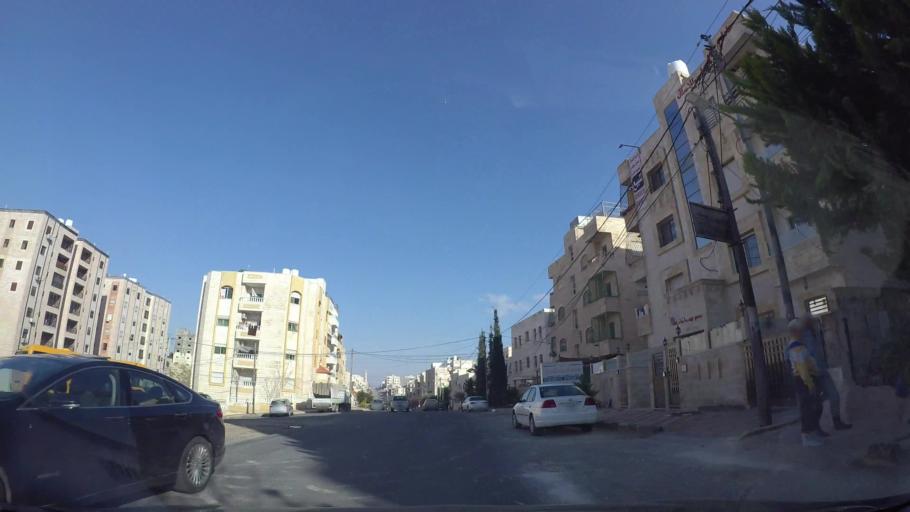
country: JO
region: Amman
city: Amman
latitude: 31.9805
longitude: 35.9498
